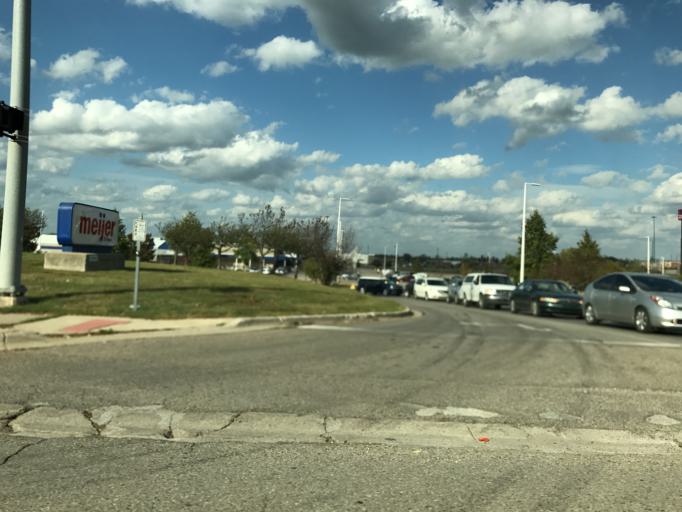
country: US
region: Michigan
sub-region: Oakland County
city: Wixom
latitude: 42.4954
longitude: -83.5405
